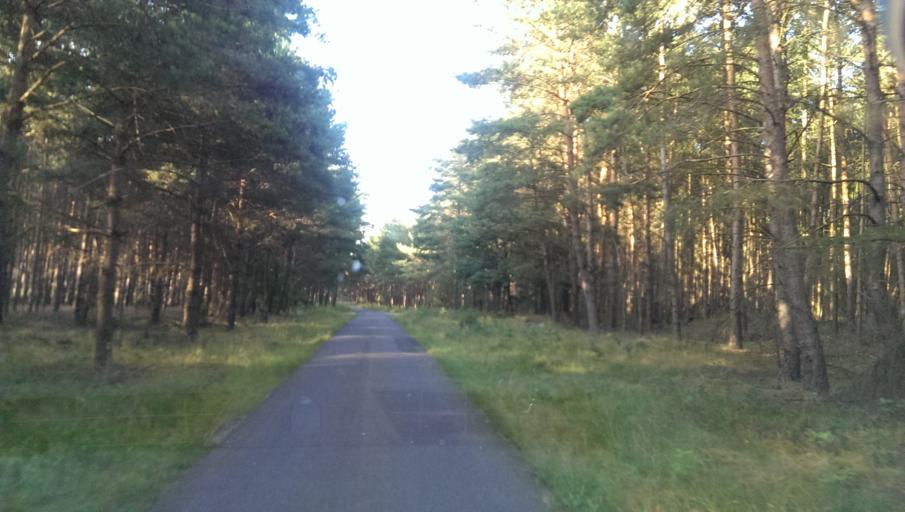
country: DE
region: Brandenburg
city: Treuenbrietzen
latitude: 52.0339
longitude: 12.8583
